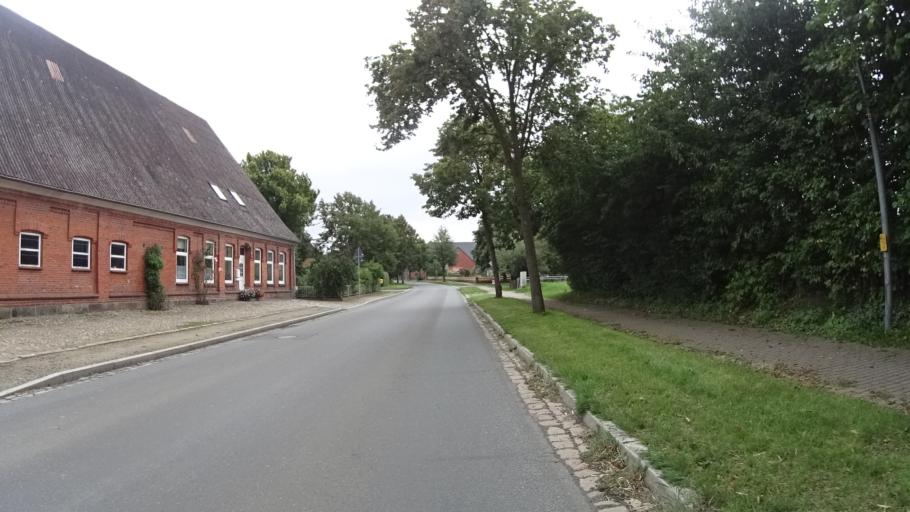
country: DE
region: Schleswig-Holstein
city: Duvensee
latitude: 53.6937
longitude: 10.5683
